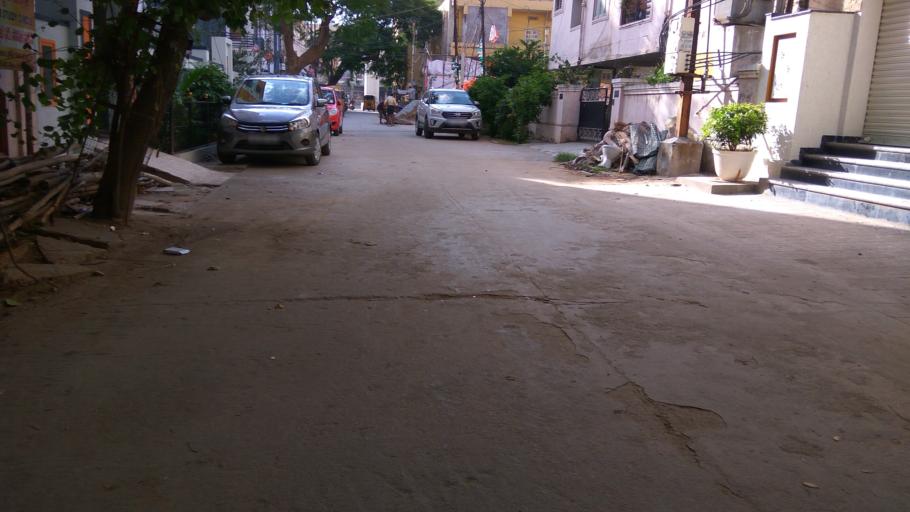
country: IN
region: Telangana
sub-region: Hyderabad
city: Hyderabad
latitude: 17.4039
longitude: 78.4965
